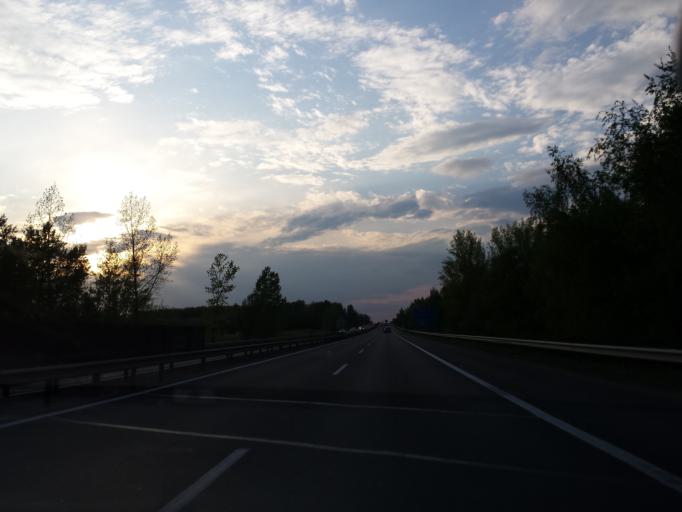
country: HU
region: Gyor-Moson-Sopron
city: Gyor
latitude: 47.6497
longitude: 17.6074
